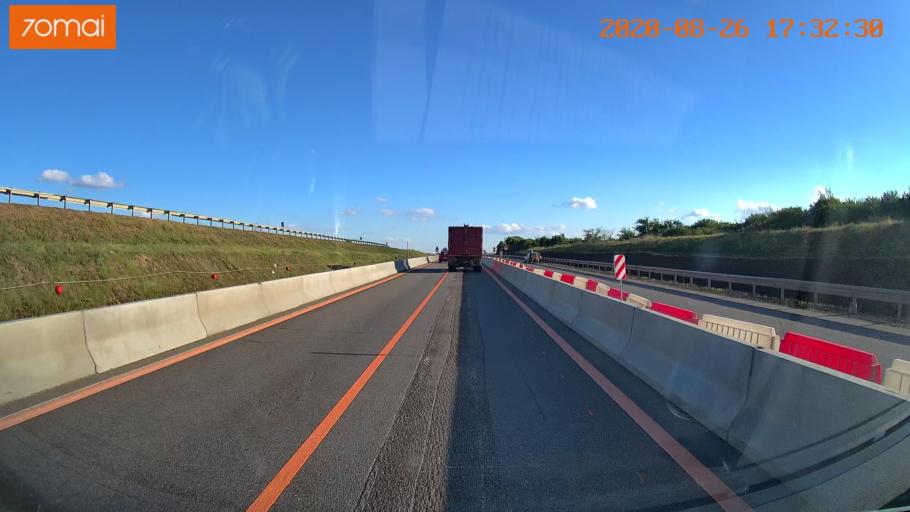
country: RU
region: Tula
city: Kazachka
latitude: 53.4213
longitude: 38.1810
